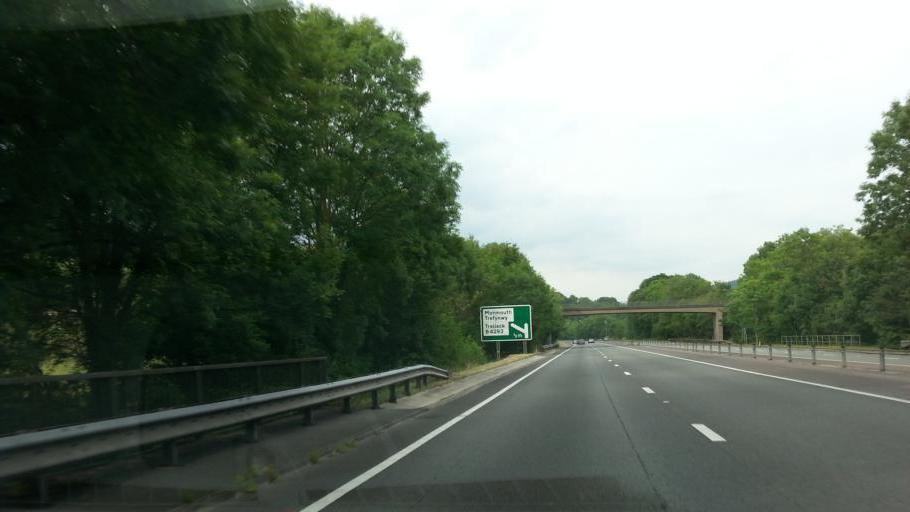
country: GB
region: Wales
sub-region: Monmouthshire
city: Mitchel Troy
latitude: 51.7978
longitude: -2.7249
